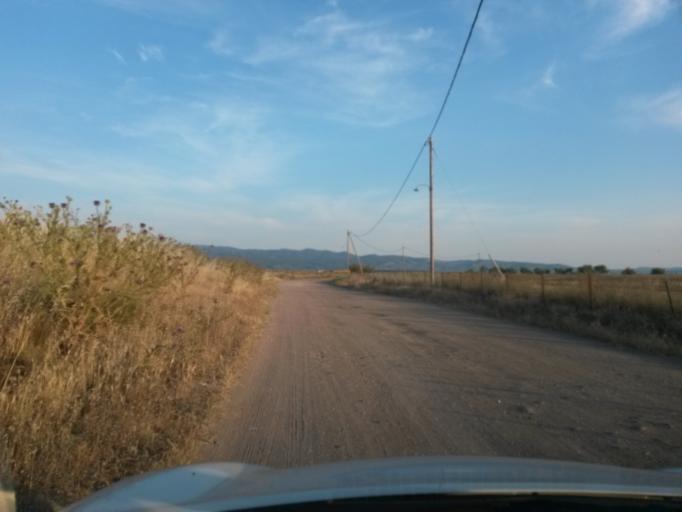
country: GR
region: North Aegean
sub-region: Nomos Lesvou
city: Kalloni
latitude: 39.2090
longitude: 26.2452
